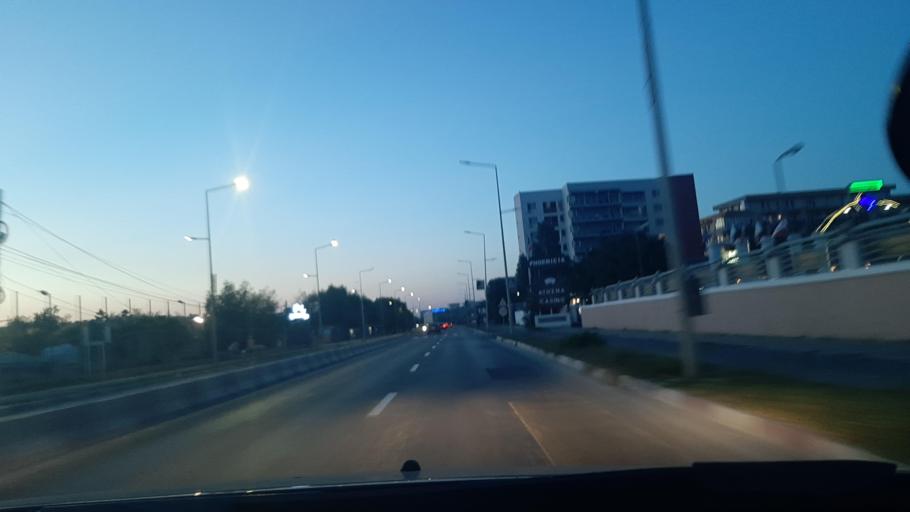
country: RO
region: Constanta
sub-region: Comuna Navodari
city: Navodari
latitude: 44.2800
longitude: 28.6177
